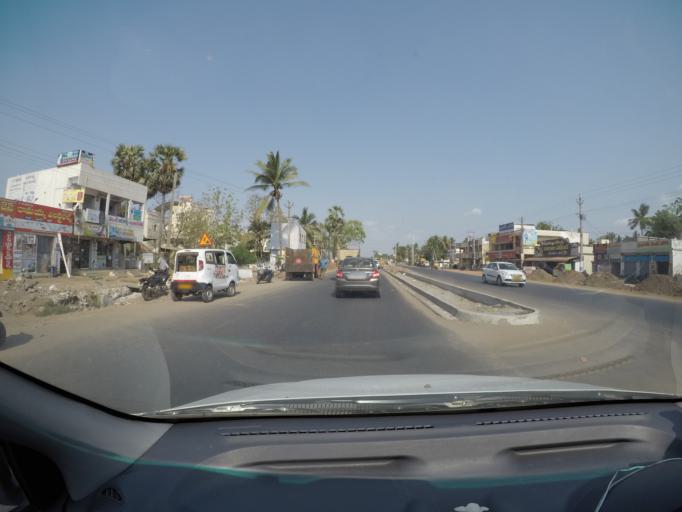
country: IN
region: Andhra Pradesh
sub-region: Krishna
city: Yanamalakuduru
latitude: 16.4761
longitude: 80.7075
